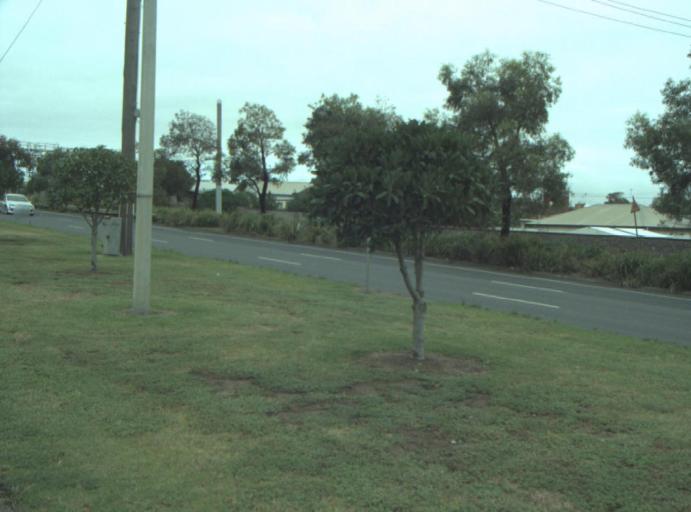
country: AU
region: Victoria
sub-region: Greater Geelong
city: Geelong West
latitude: -38.1287
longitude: 144.3516
